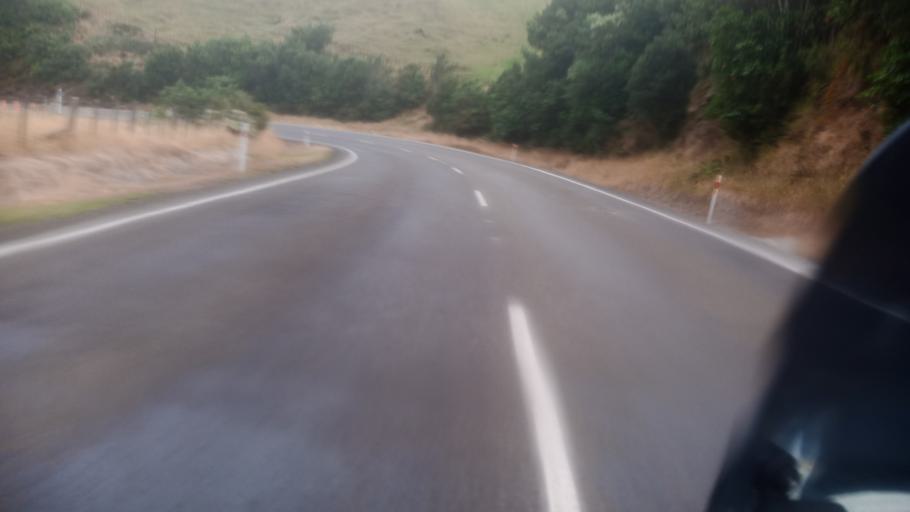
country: NZ
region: Bay of Plenty
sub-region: Opotiki District
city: Opotiki
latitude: -38.3564
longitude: 177.4522
